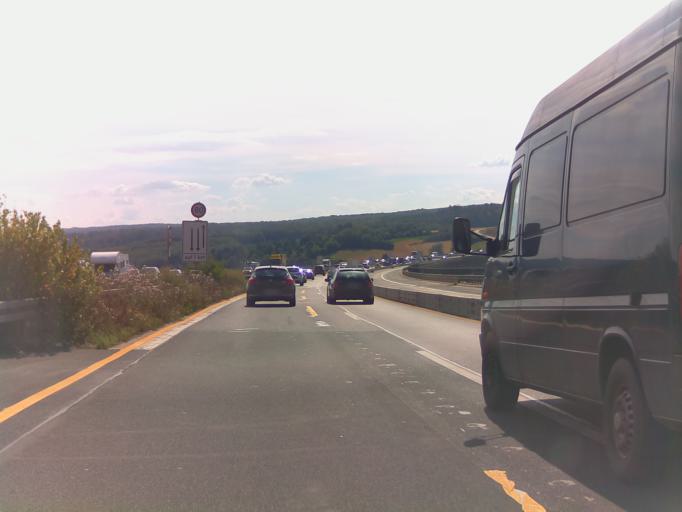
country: DE
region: Bavaria
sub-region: Regierungsbezirk Unterfranken
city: Randersacker
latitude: 49.7536
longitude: 9.9473
